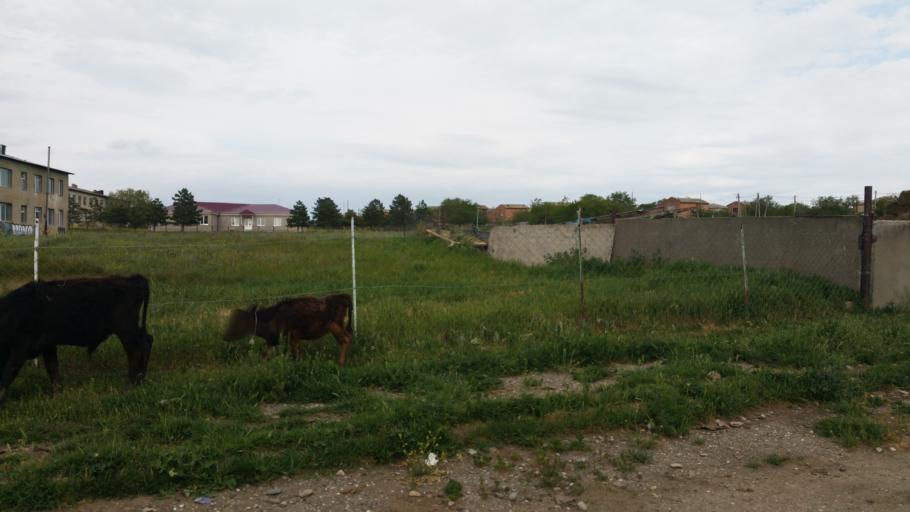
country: AZ
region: Agstafa
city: Saloglu
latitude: 41.5046
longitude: 45.3770
